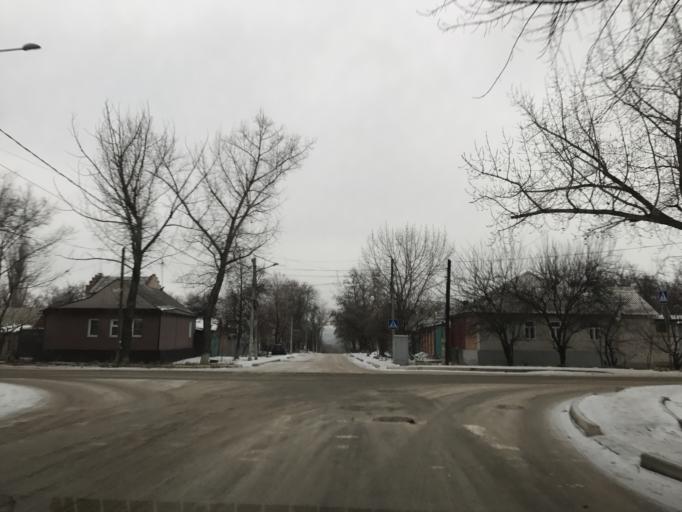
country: RU
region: Rostov
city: Kamensk-Shakhtinskiy
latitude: 48.3307
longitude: 40.2649
